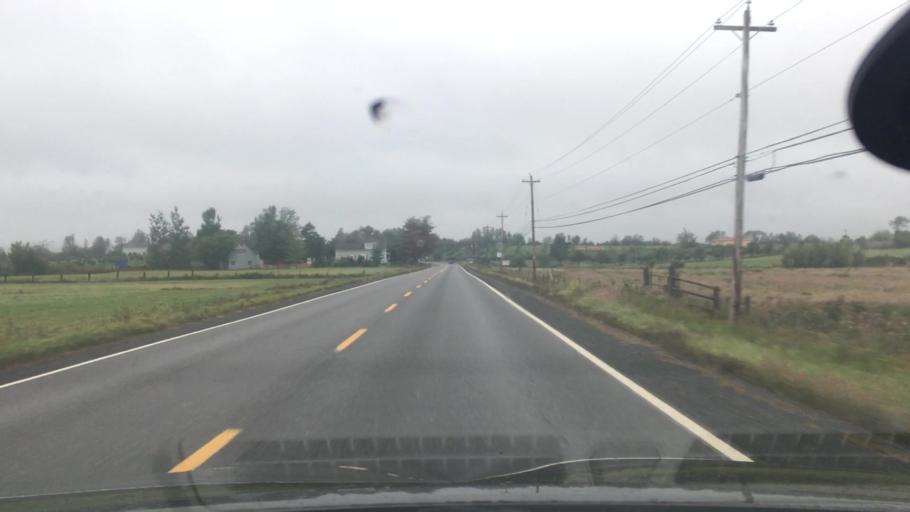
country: CA
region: Nova Scotia
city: Windsor
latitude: 44.9509
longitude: -64.1676
